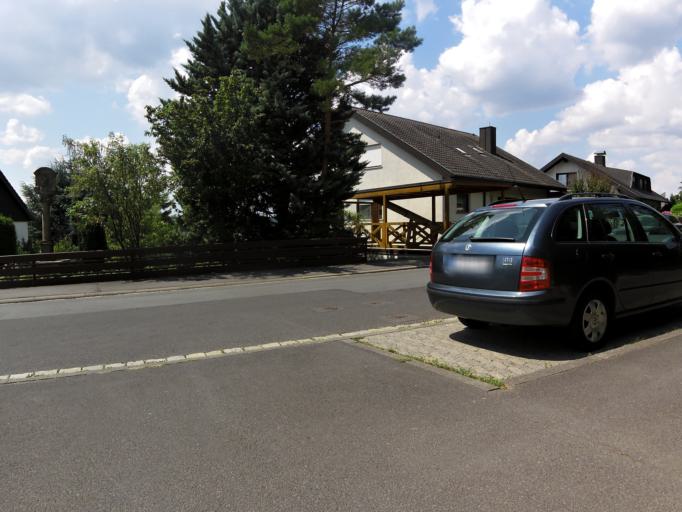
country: DE
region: Bavaria
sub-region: Regierungsbezirk Unterfranken
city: Randersacker
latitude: 49.7515
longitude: 9.9530
